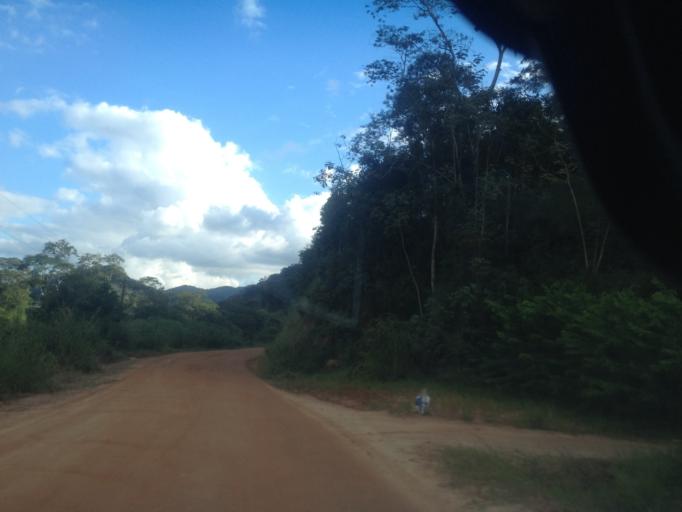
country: BR
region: Rio de Janeiro
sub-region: Quatis
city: Quatis
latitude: -22.2347
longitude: -44.2596
